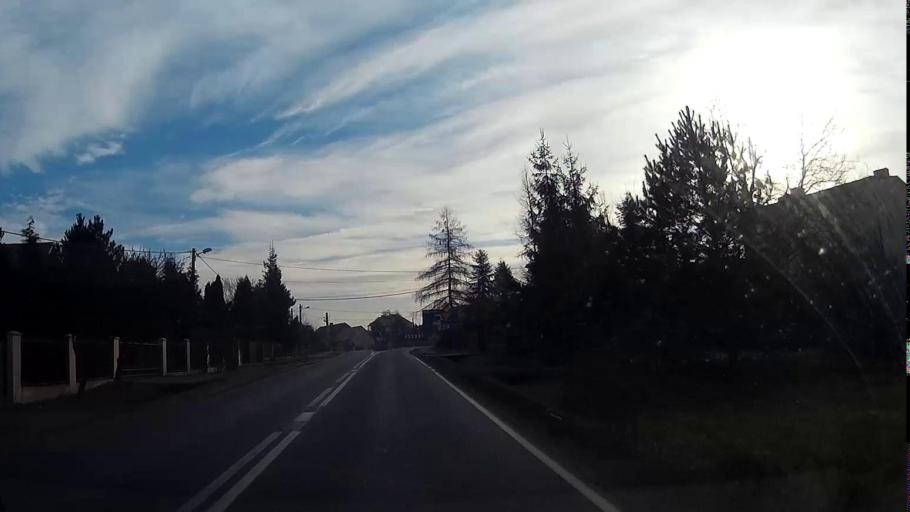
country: PL
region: Lesser Poland Voivodeship
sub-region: Powiat krakowski
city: Liszki
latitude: 50.0344
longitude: 19.7544
